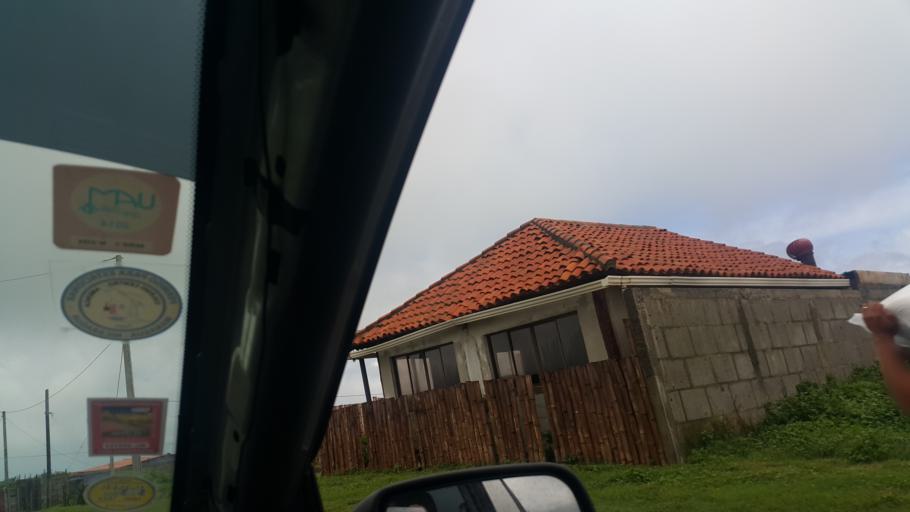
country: NI
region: Managua
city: El Crucero
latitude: 11.9551
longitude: -86.3022
